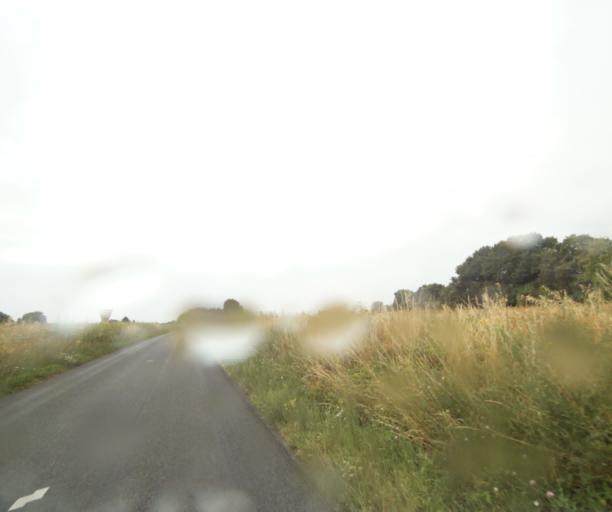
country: FR
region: Ile-de-France
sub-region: Departement de Seine-et-Marne
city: Saint-Sauveur-sur-Ecole
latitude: 48.4869
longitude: 2.5487
